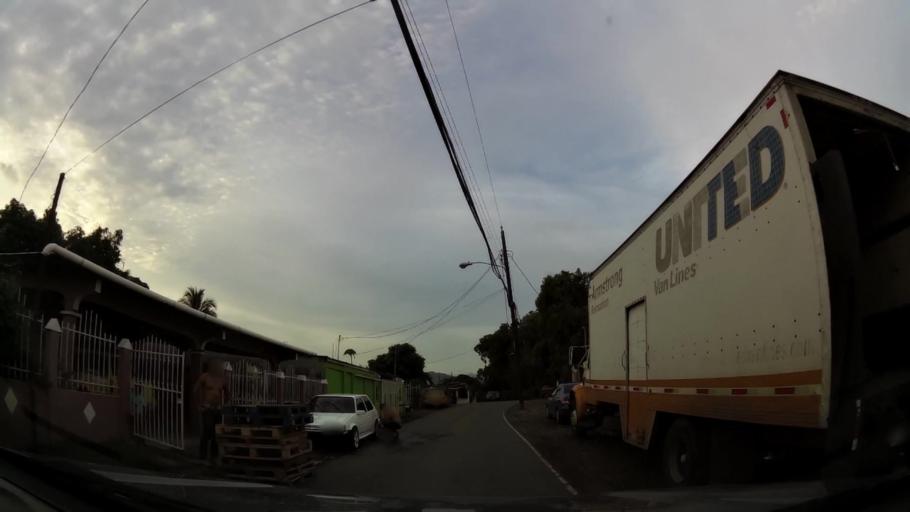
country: PA
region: Panama
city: Tocumen
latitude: 9.0884
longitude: -79.3895
